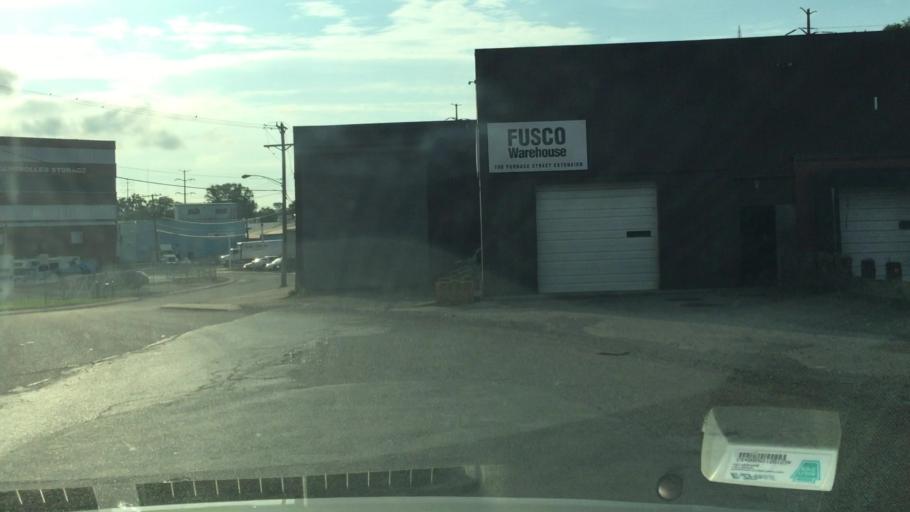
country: US
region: Pennsylvania
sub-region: Allegheny County
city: McKees Rocks
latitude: 40.4634
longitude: -80.0658
